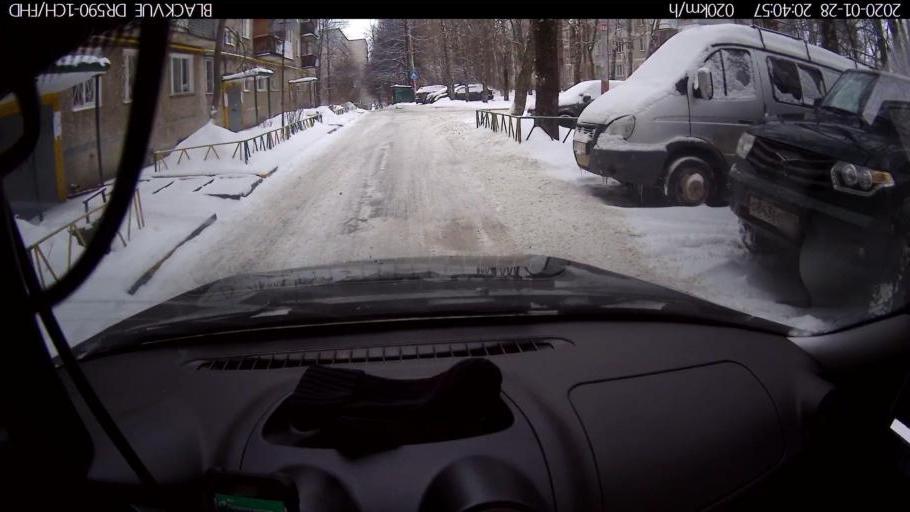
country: RU
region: Nizjnij Novgorod
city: Nizhniy Novgorod
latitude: 56.2306
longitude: 43.9540
